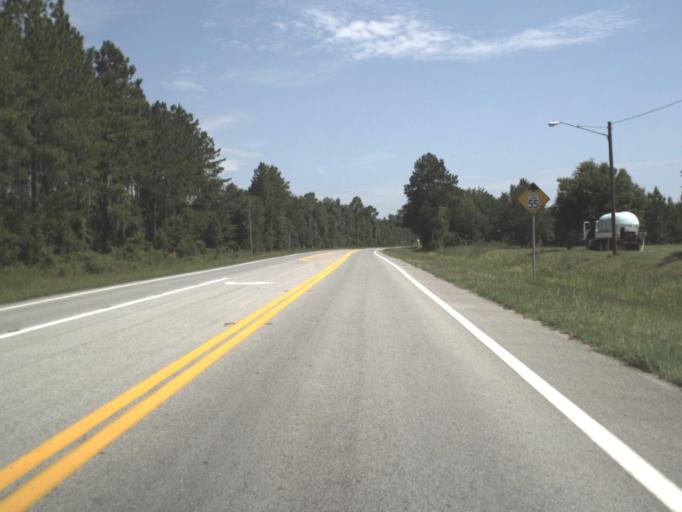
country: US
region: Florida
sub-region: Hamilton County
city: Jasper
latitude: 30.4390
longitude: -82.9338
